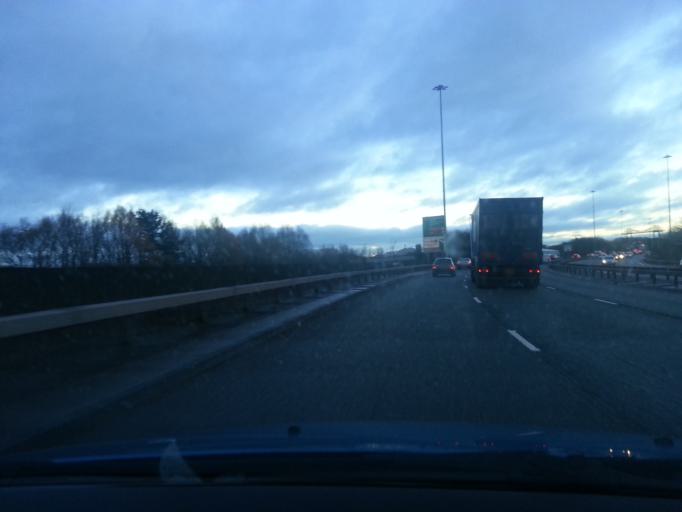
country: GB
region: England
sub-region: Middlesbrough
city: Middlesbrough
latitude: 54.5747
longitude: -1.2547
